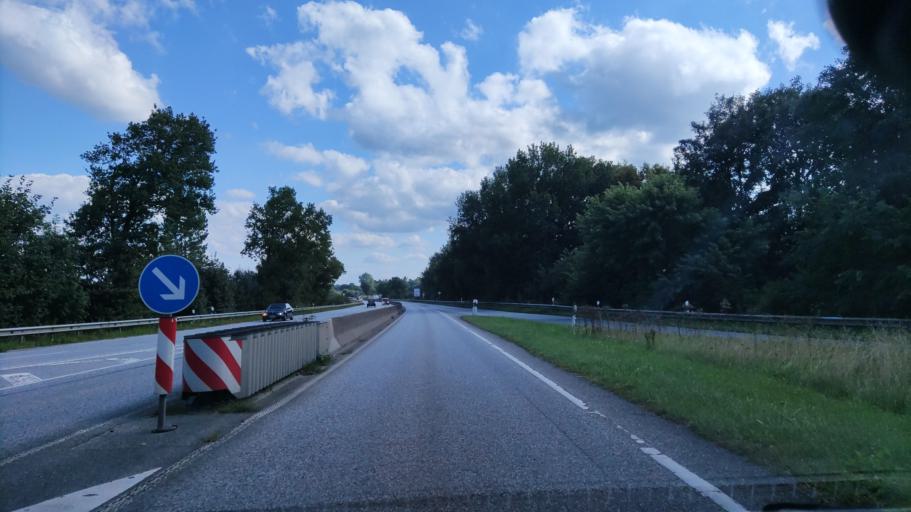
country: DE
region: Schleswig-Holstein
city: Fockbek
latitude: 54.3088
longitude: 9.6288
